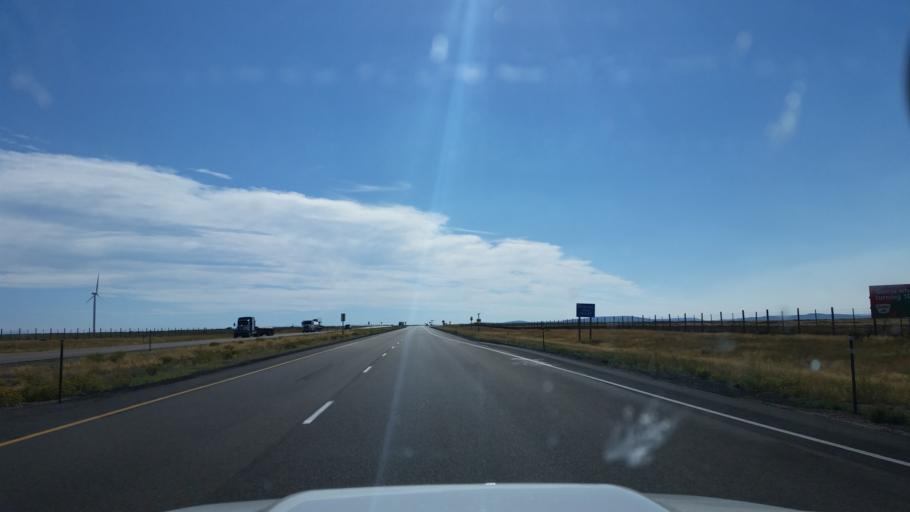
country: US
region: Wyoming
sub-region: Uinta County
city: Mountain View
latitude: 41.3009
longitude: -110.5448
